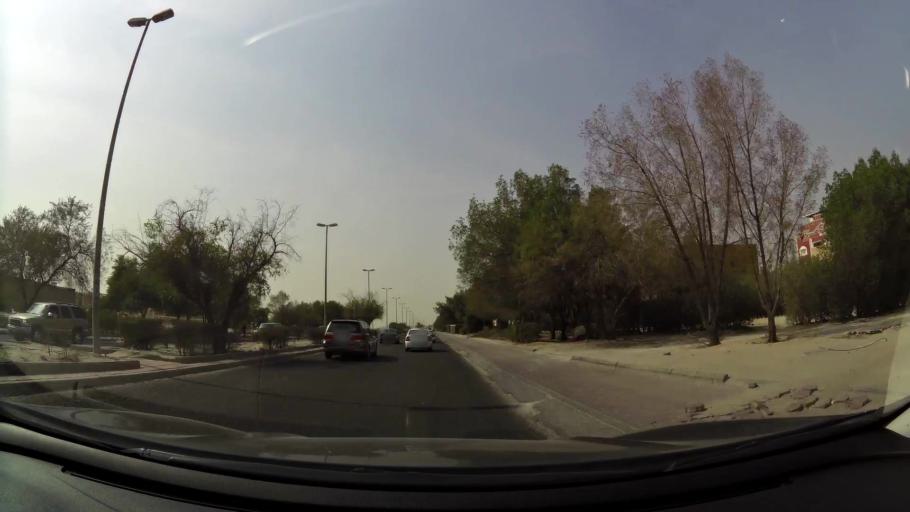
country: KW
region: Al Farwaniyah
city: Al Farwaniyah
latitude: 29.2483
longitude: 47.9385
